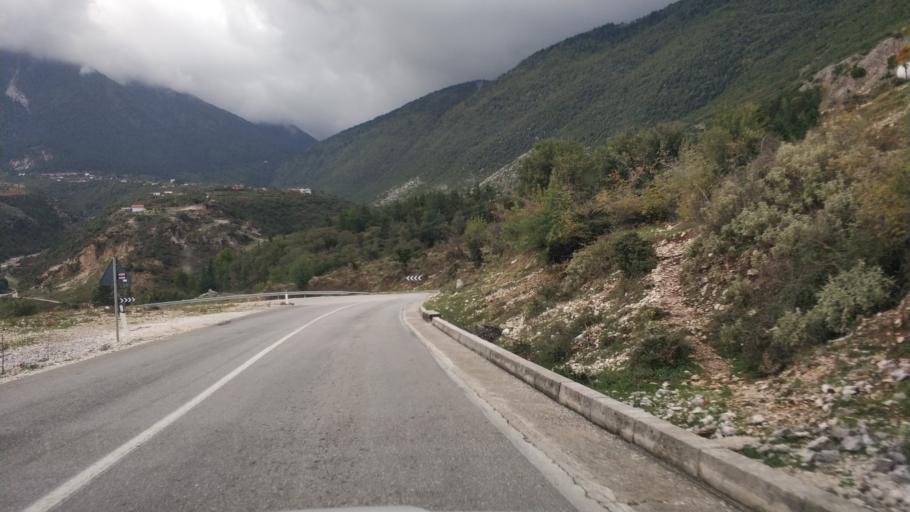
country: AL
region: Vlore
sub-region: Rrethi i Vlores
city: Orikum
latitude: 40.2420
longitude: 19.5508
